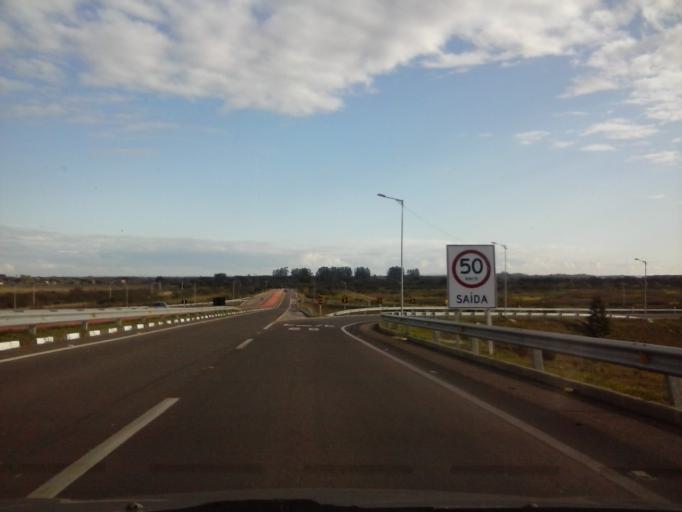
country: BR
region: Rio Grande do Sul
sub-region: Canoas
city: Canoas
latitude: -29.9235
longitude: -51.2299
